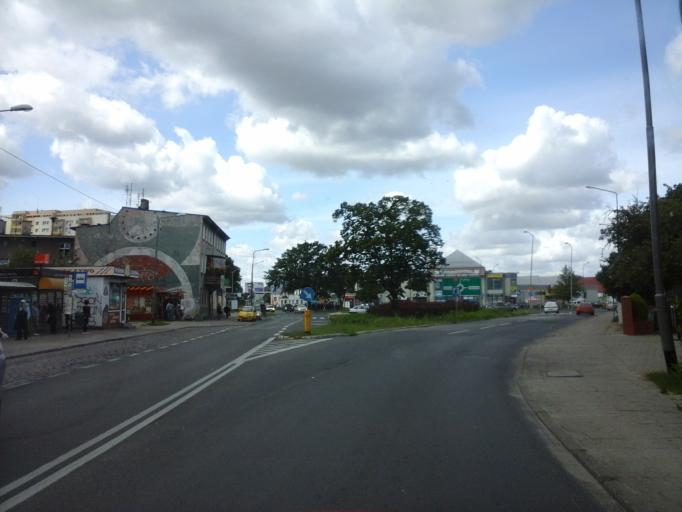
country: PL
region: West Pomeranian Voivodeship
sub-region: Szczecin
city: Szczecin
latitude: 53.3833
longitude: 14.6353
